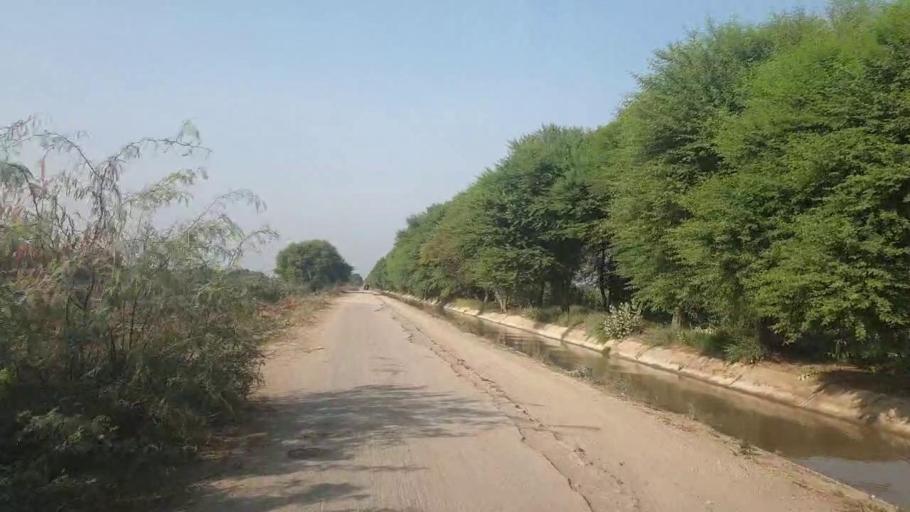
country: PK
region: Sindh
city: Tando Jam
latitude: 25.4223
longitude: 68.4620
